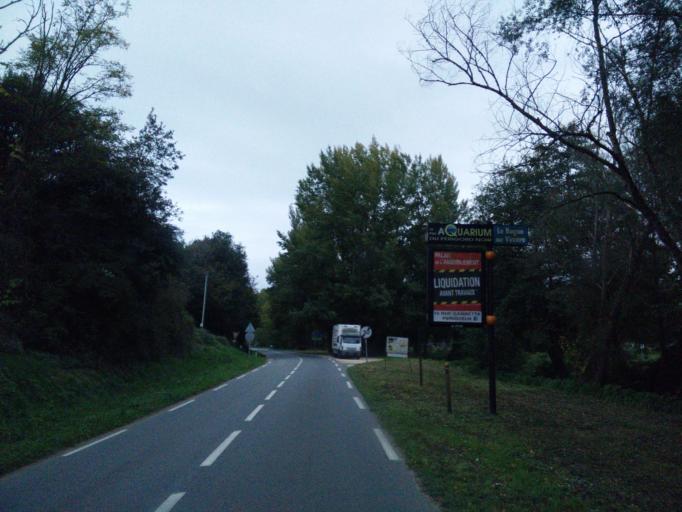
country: FR
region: Aquitaine
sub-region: Departement de la Dordogne
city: Carsac-Aillac
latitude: 44.8055
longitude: 1.2976
